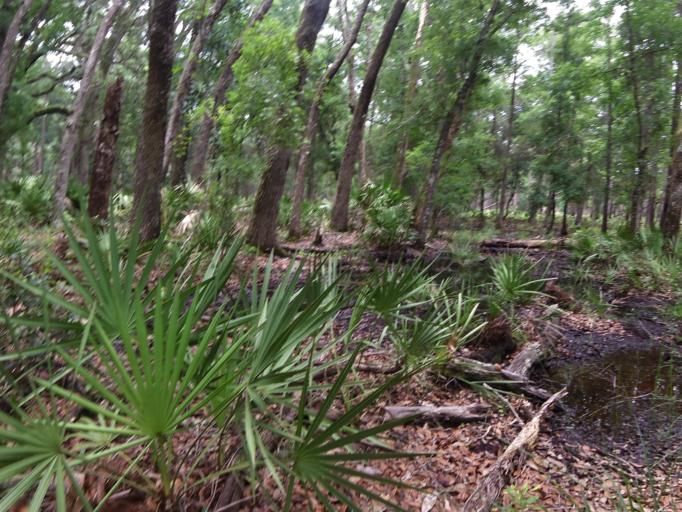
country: US
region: Florida
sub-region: Clay County
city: Green Cove Springs
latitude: 29.9732
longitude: -81.6373
